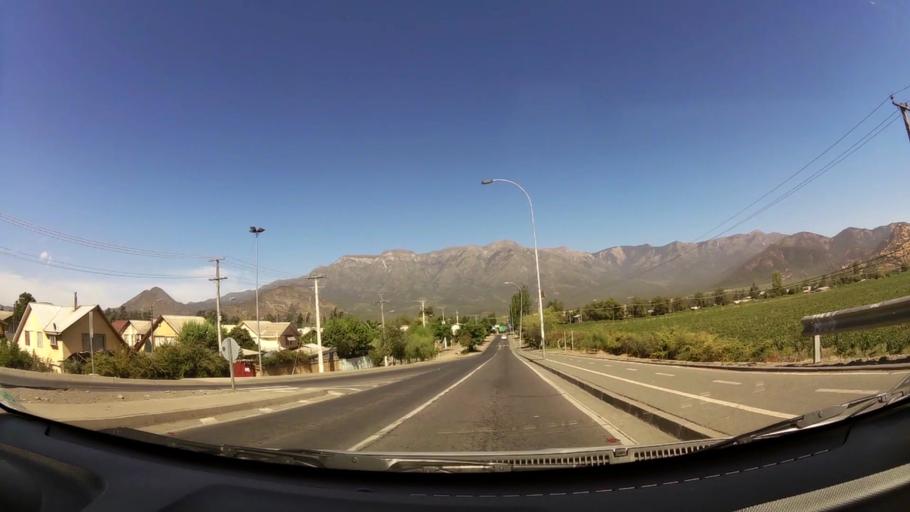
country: CL
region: O'Higgins
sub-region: Provincia de Cachapoal
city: Graneros
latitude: -33.9675
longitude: -70.7094
